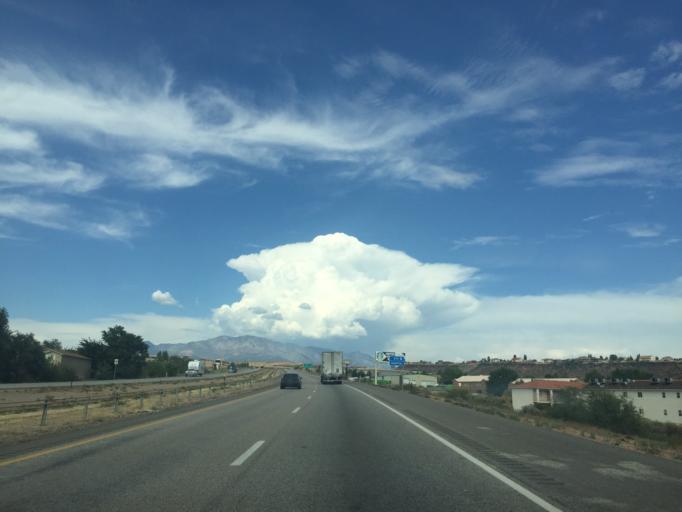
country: US
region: Utah
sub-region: Washington County
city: Saint George
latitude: 37.1011
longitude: -113.5613
